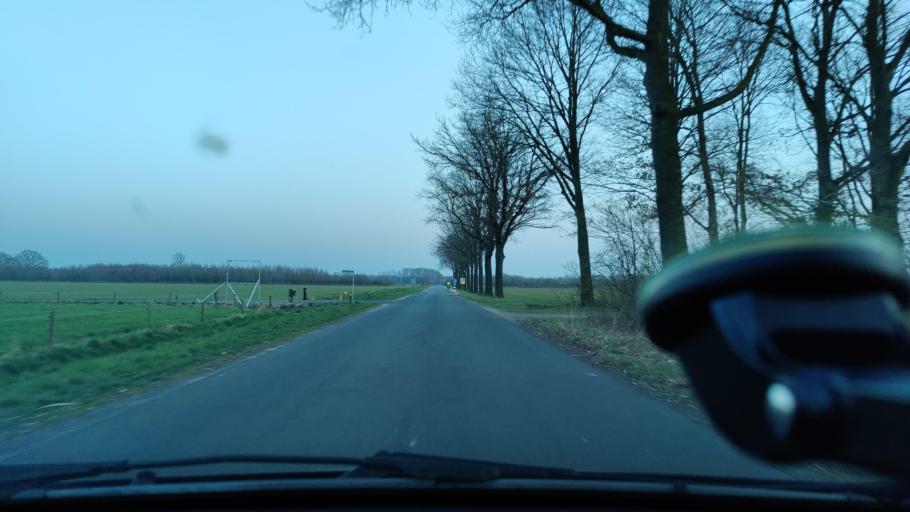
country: NL
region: Limburg
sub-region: Gemeente Bergen
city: Wellerlooi
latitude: 51.5377
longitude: 6.1734
